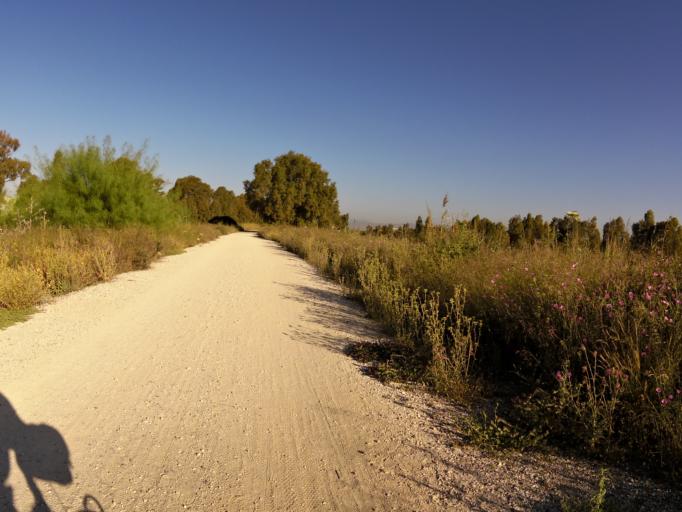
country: ES
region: Andalusia
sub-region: Provincia de Malaga
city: Torremolinos
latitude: 36.6740
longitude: -4.4678
